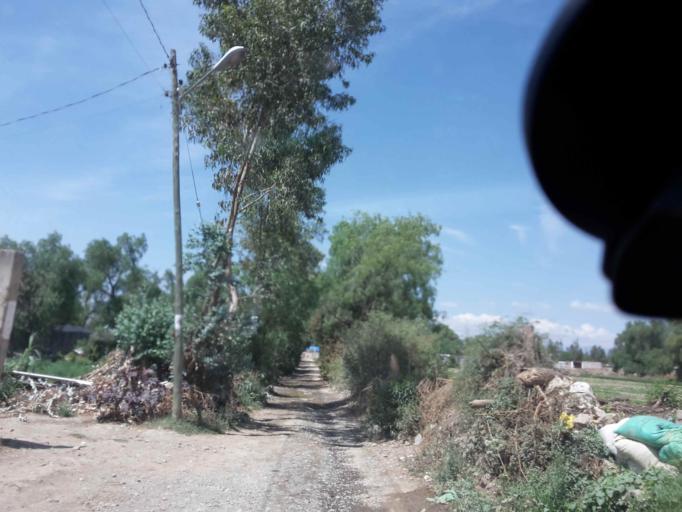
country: BO
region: Cochabamba
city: Cochabamba
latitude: -17.3611
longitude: -66.2224
